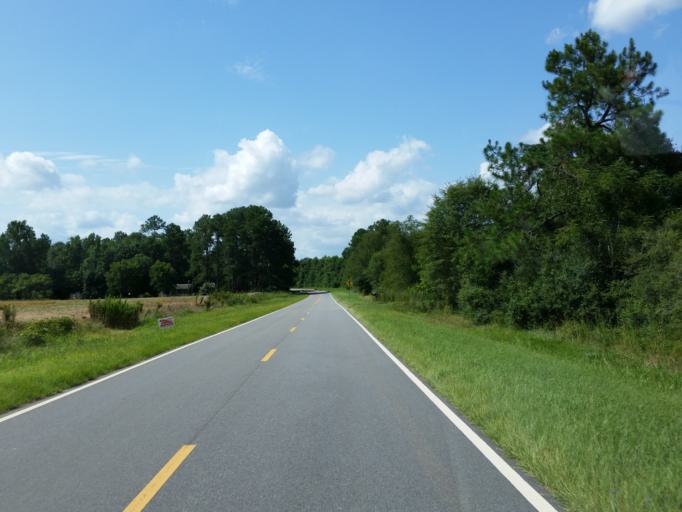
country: US
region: Georgia
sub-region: Tift County
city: Tifton
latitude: 31.6036
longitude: -83.4754
